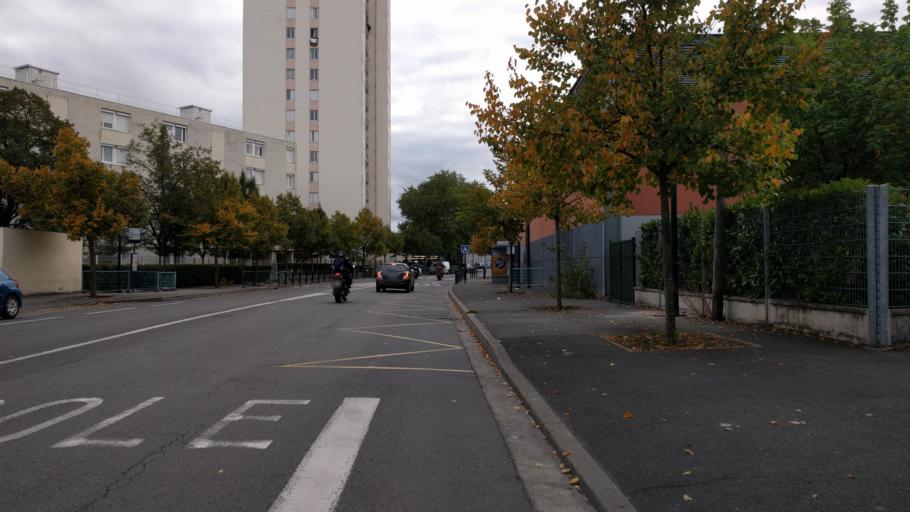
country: FR
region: Aquitaine
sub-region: Departement de la Gironde
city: Bordeaux
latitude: 44.8645
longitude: -0.5640
